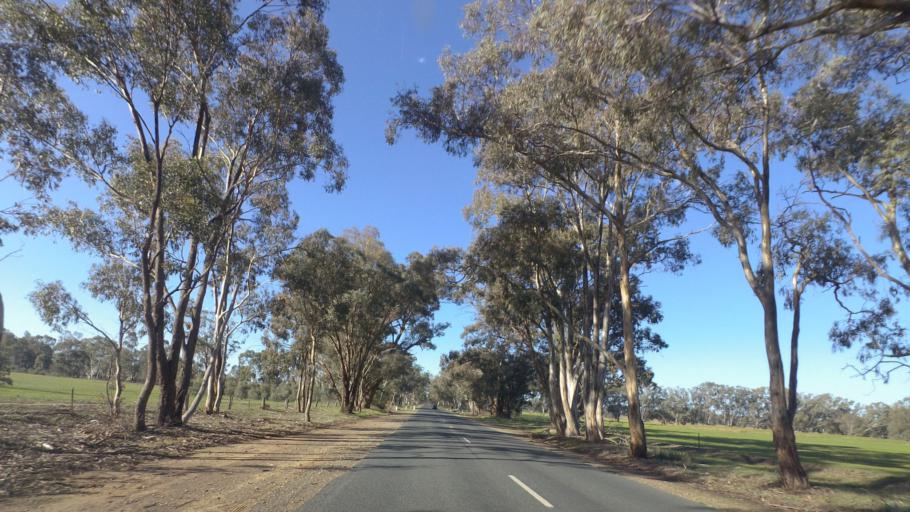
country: AU
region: Victoria
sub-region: Greater Bendigo
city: Epsom
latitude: -36.6613
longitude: 144.4591
